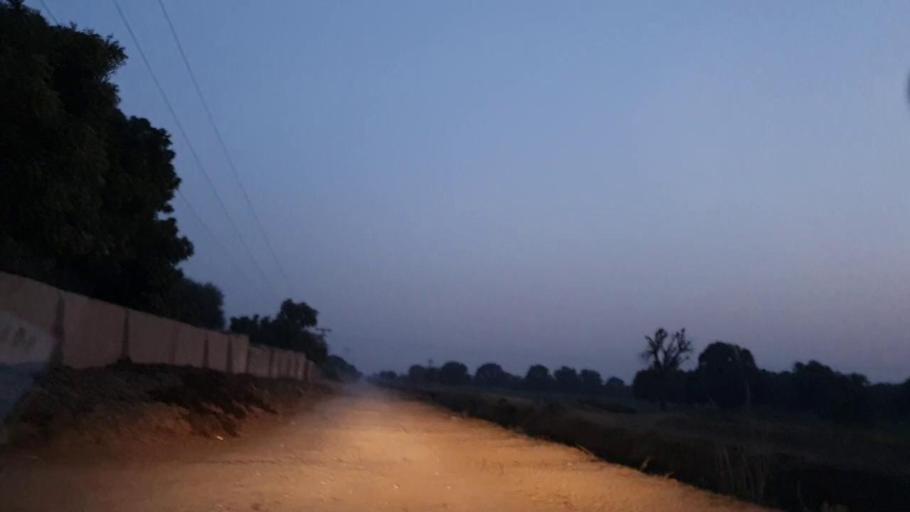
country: PK
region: Sindh
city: Tando Ghulam Ali
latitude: 25.1029
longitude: 68.9106
